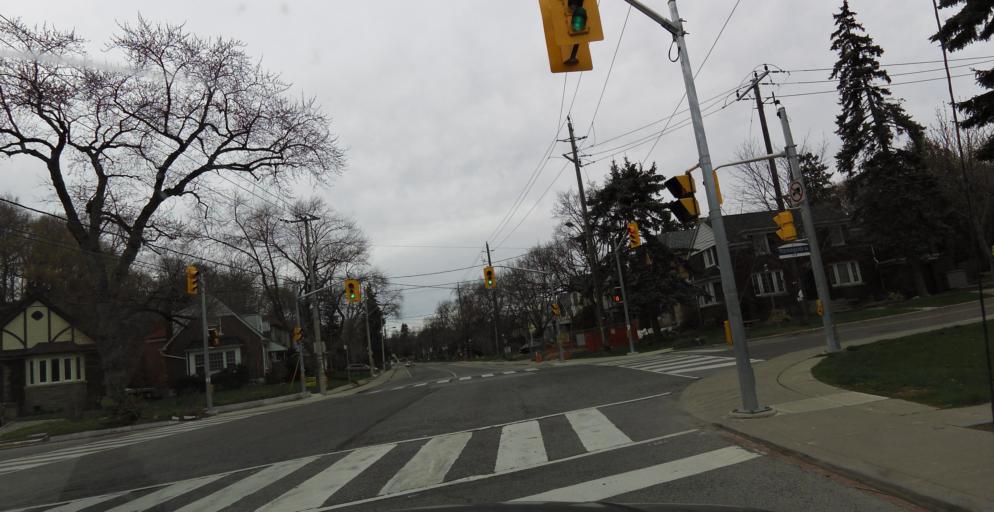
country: CA
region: Ontario
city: Etobicoke
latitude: 43.6439
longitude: -79.4819
